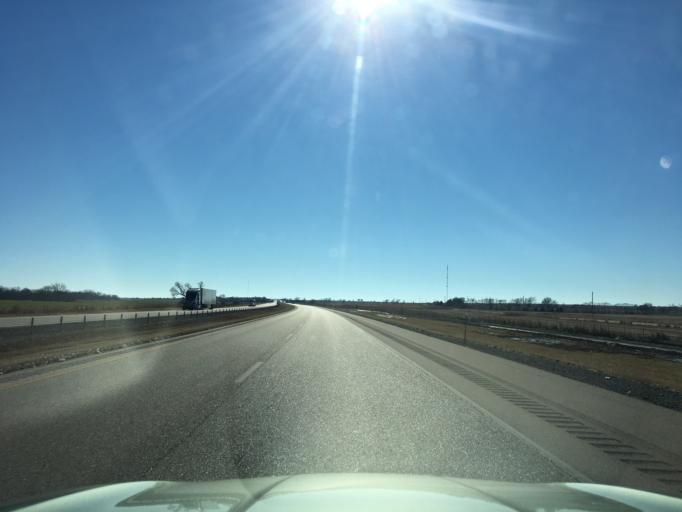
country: US
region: Oklahoma
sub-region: Kay County
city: Blackwell
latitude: 36.8956
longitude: -97.3541
